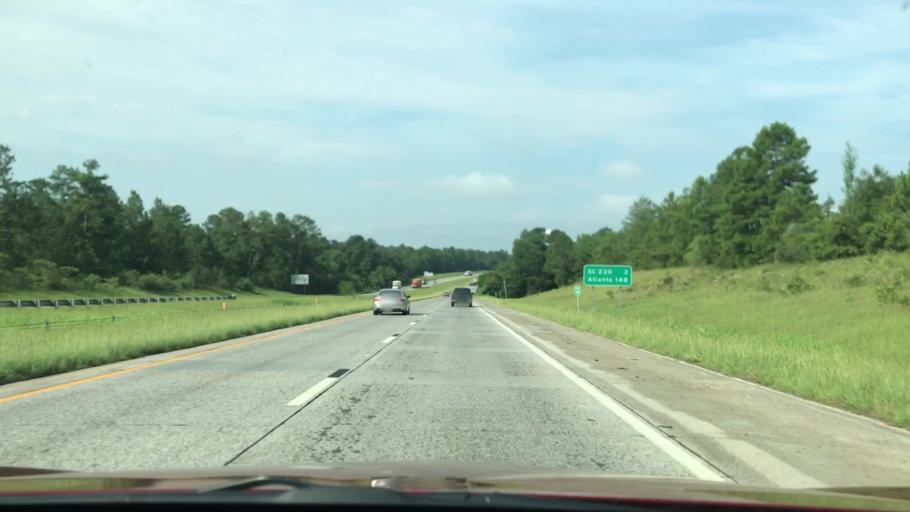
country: US
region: South Carolina
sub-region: Aiken County
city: Belvedere
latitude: 33.5550
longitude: -81.9482
